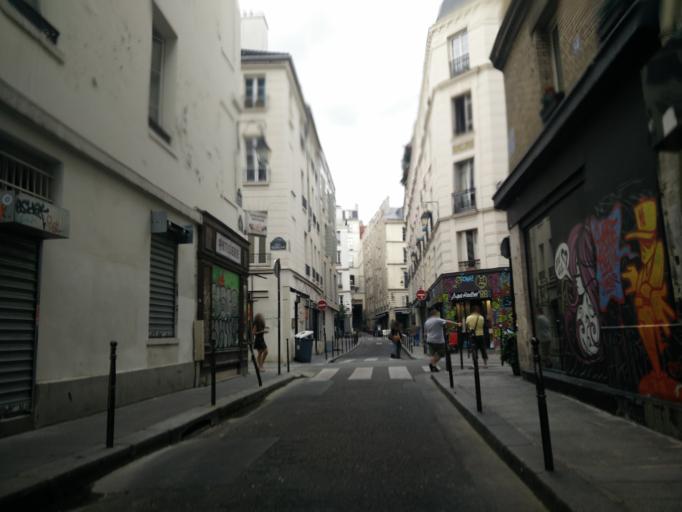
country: FR
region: Ile-de-France
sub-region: Paris
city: Paris
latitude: 48.8667
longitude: 2.3582
